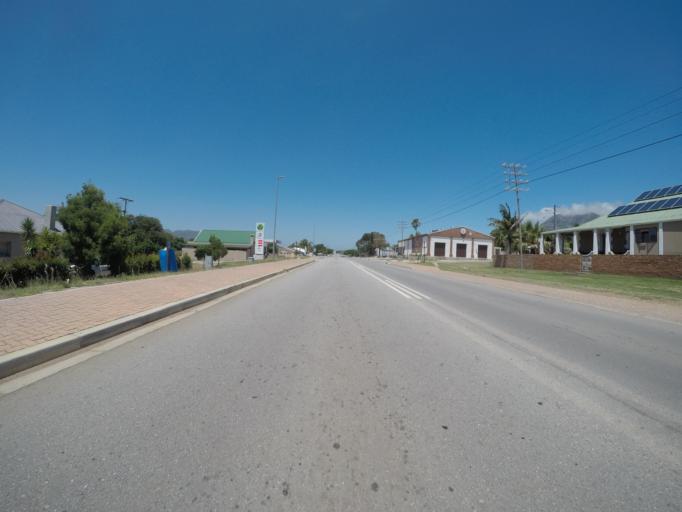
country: ZA
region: Eastern Cape
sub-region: Cacadu District Municipality
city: Kareedouw
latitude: -33.9514
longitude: 24.2877
